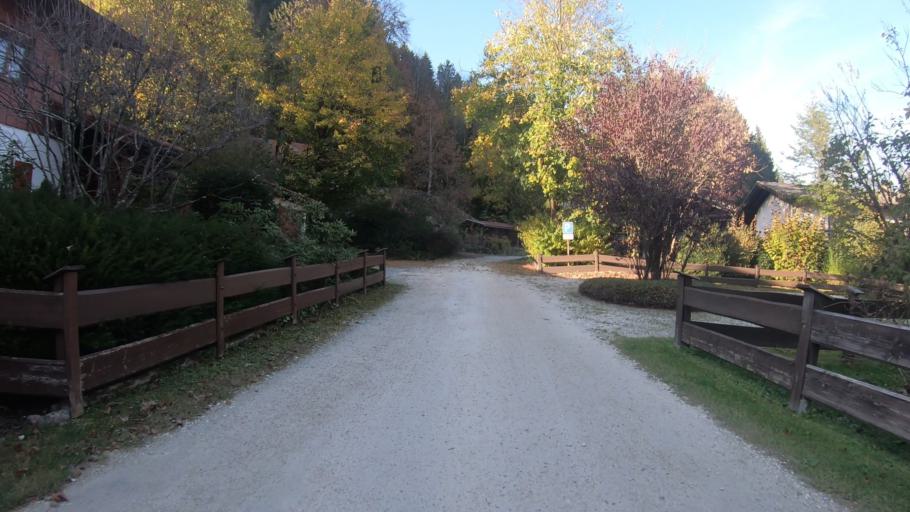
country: DE
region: Bavaria
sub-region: Upper Bavaria
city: Bergen
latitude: 47.8101
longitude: 12.5860
